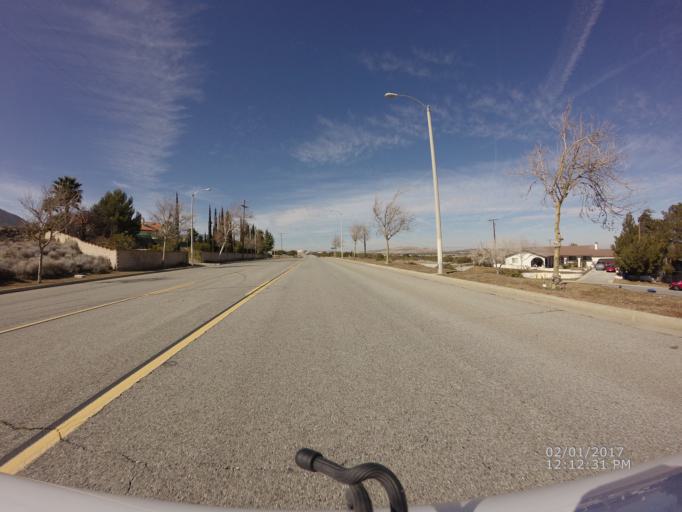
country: US
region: California
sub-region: Los Angeles County
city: Palmdale
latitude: 34.5454
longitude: -118.1236
